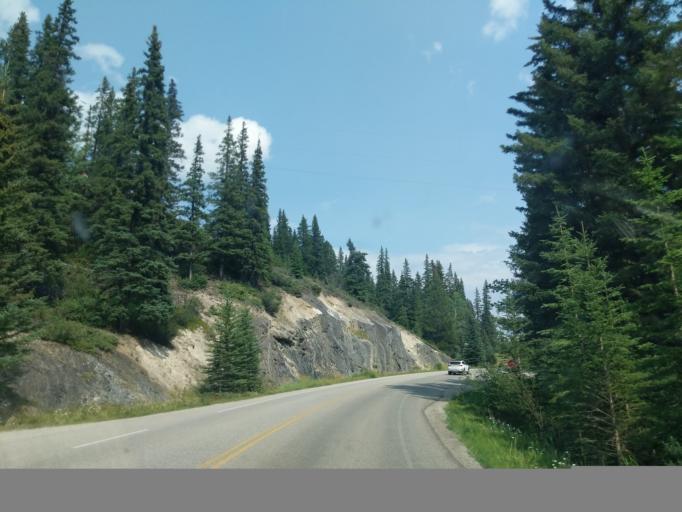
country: CA
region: Alberta
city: Banff
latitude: 51.1685
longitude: -115.6873
